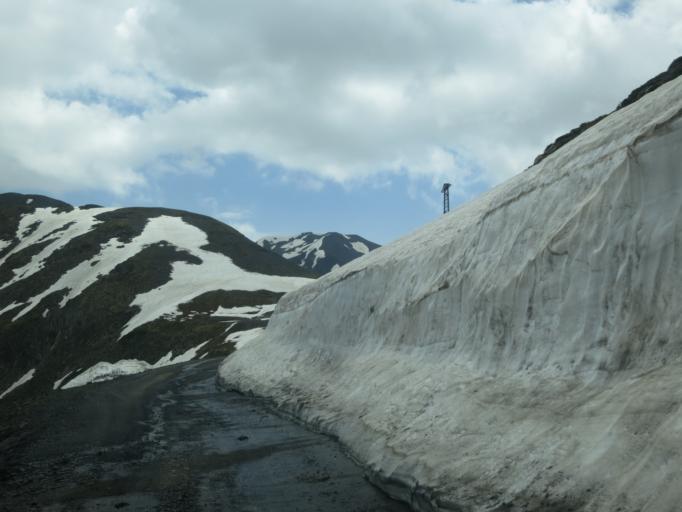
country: GE
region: Kakheti
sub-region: Telavi
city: Telavi
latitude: 42.2798
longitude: 45.5049
